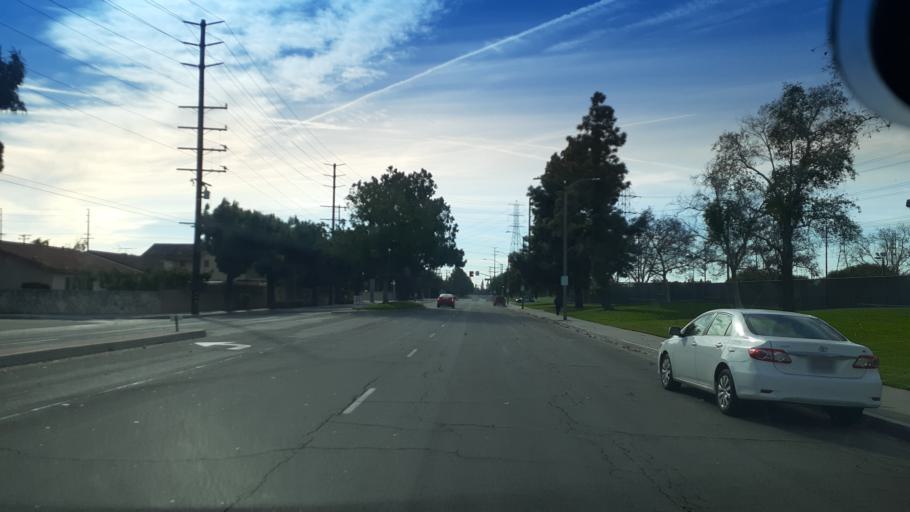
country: US
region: California
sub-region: Los Angeles County
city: Artesia
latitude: 33.8550
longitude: -118.0997
